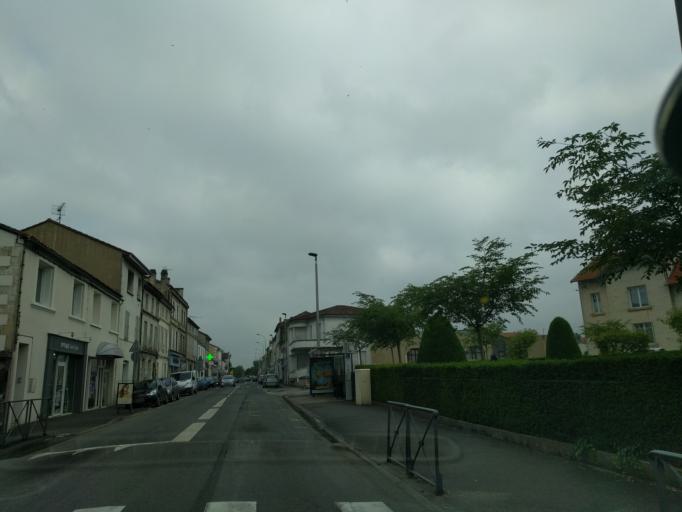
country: FR
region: Poitou-Charentes
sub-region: Departement de la Charente
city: Angouleme
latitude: 45.6573
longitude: 0.1472
